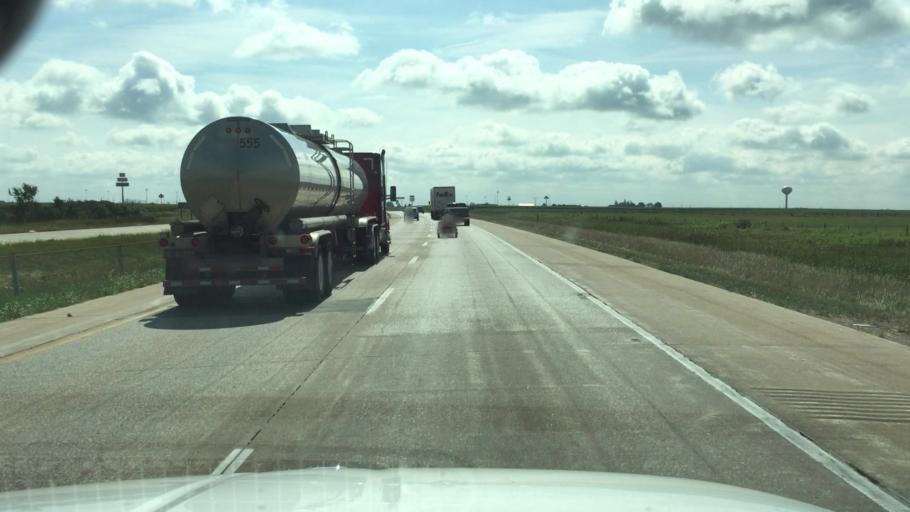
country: US
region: Iowa
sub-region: Scott County
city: Walcott
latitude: 41.6194
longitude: -90.7989
